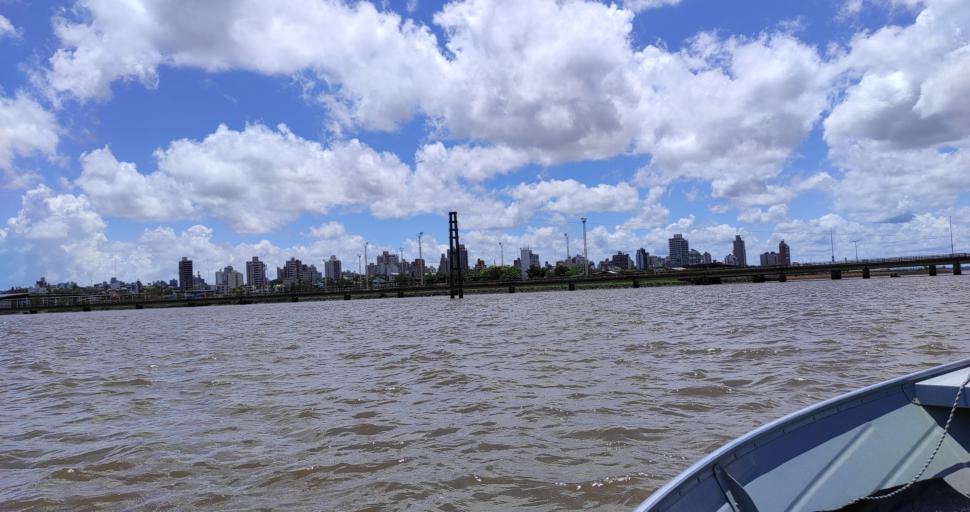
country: AR
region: Misiones
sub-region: Departamento de Capital
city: Posadas
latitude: -27.3780
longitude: -55.8792
